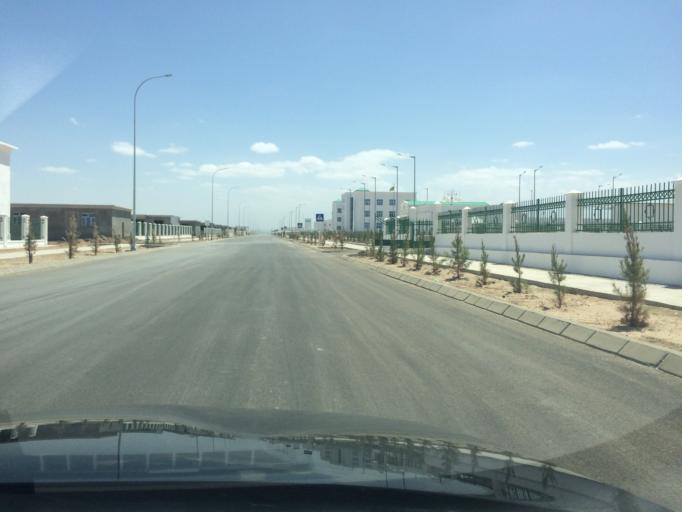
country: TM
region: Ahal
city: Abadan
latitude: 38.0999
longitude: 58.2939
